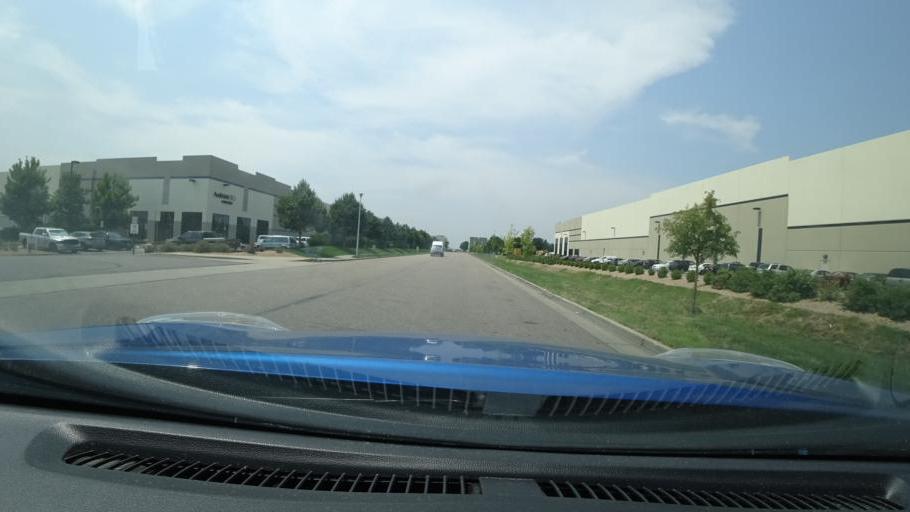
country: US
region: Colorado
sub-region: Adams County
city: Aurora
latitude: 39.7660
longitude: -104.7584
